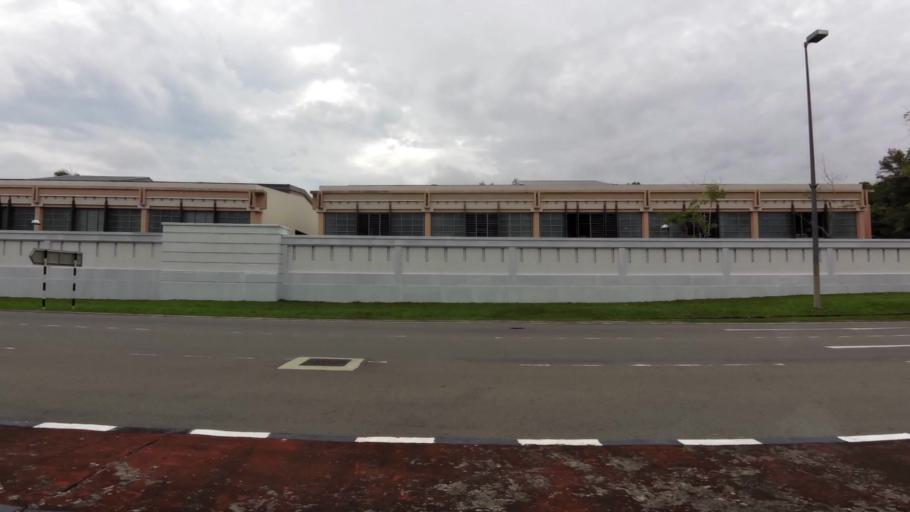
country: BN
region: Brunei and Muara
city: Bandar Seri Begawan
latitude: 4.9141
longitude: 114.9312
